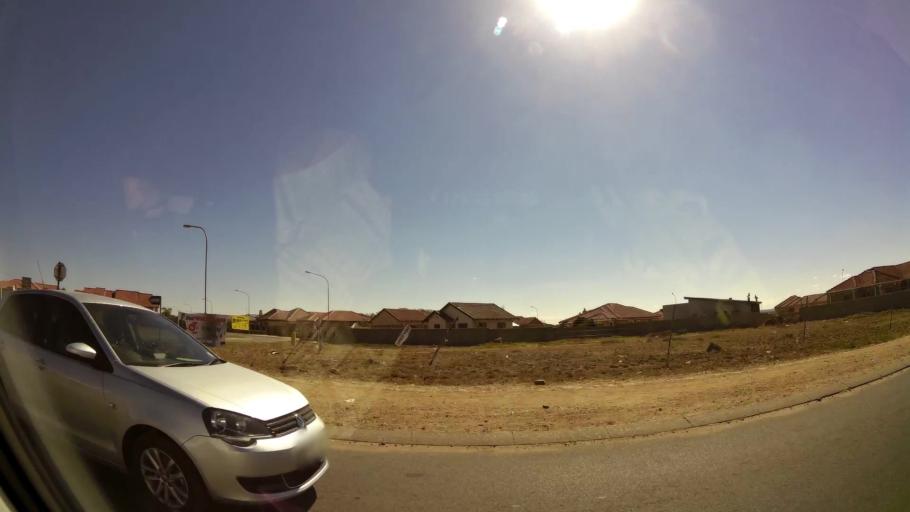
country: ZA
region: Limpopo
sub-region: Capricorn District Municipality
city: Polokwane
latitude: -23.8707
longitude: 29.4235
